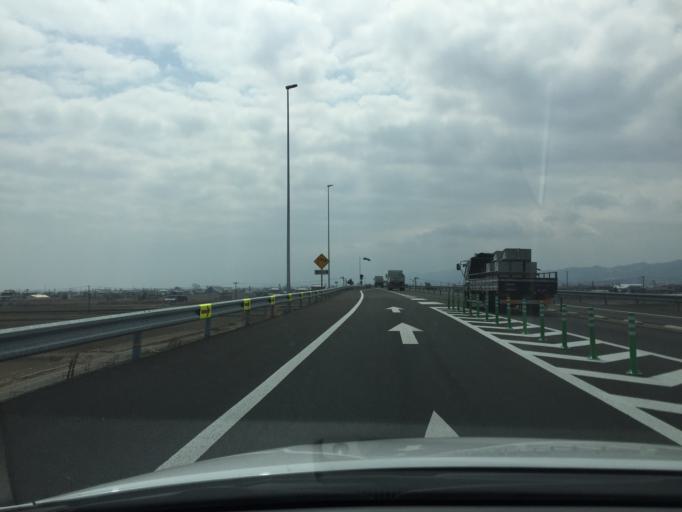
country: JP
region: Miyagi
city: Watari
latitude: 38.0364
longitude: 140.8922
